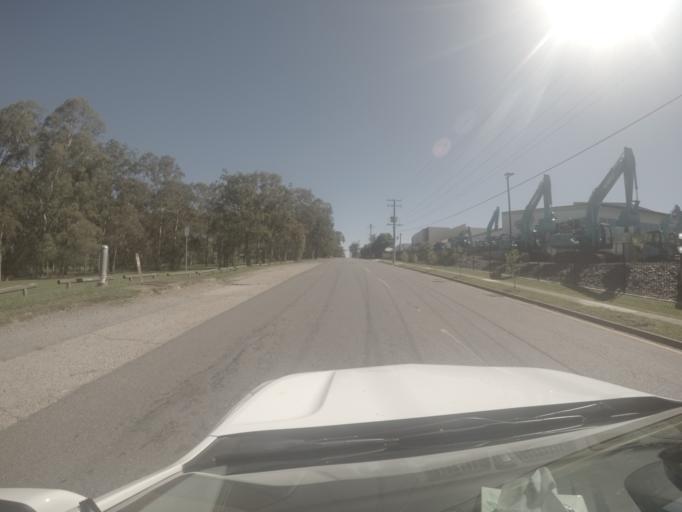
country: AU
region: Queensland
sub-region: Brisbane
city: Richlands
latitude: -27.5761
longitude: 152.9612
